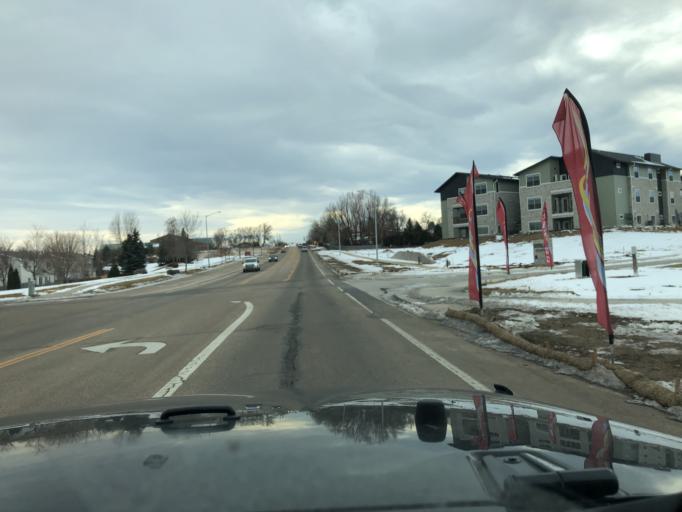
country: US
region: Colorado
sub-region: Boulder County
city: Longmont
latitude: 40.1792
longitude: -105.0742
